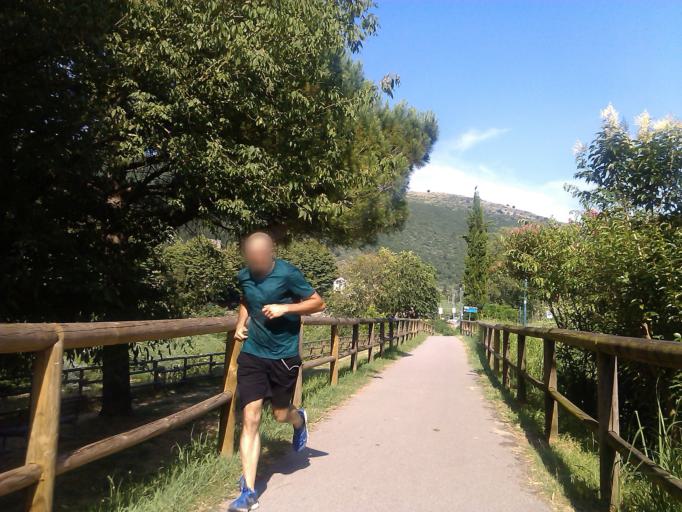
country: IT
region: Tuscany
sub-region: Provincia di Prato
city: Prato
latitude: 43.8727
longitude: 11.1136
